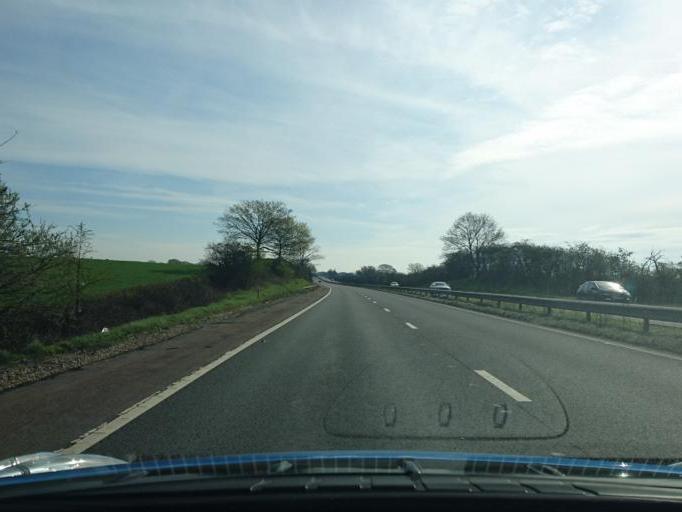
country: GB
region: England
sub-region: Herefordshire
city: Donnington
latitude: 51.9948
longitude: -2.3427
